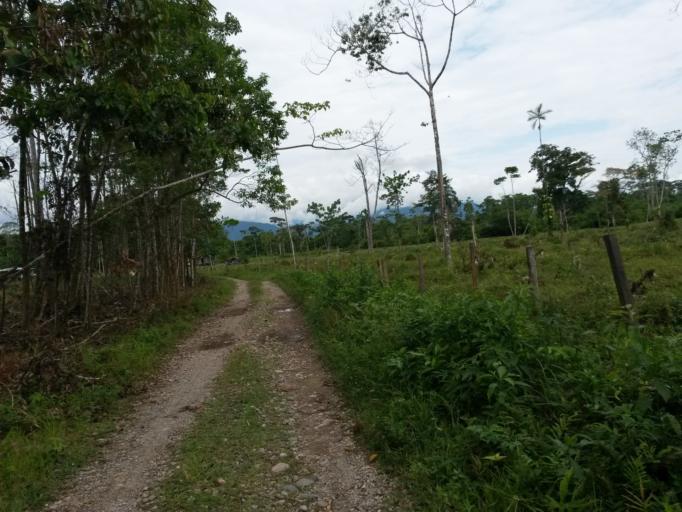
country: CO
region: Putumayo
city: Puerto Guzman
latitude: 1.0221
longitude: -76.3749
